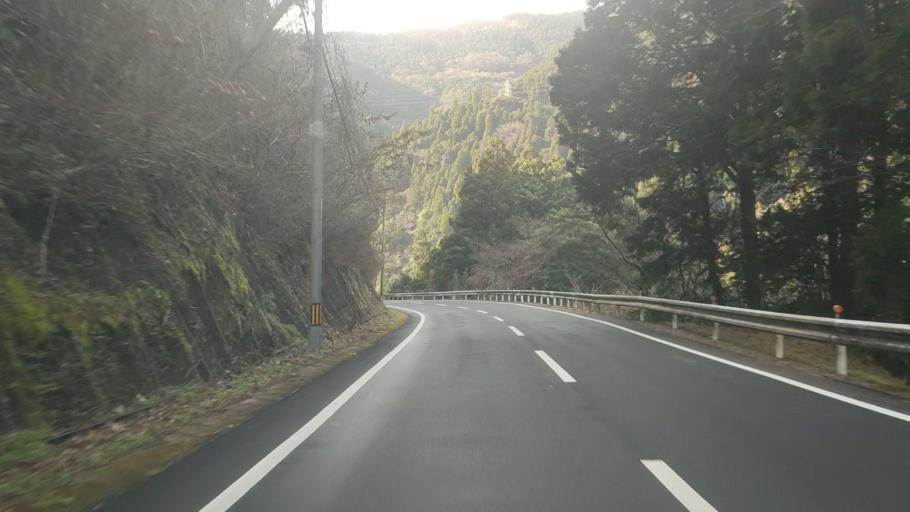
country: JP
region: Kumamoto
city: Hitoyoshi
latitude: 32.3232
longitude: 130.8405
